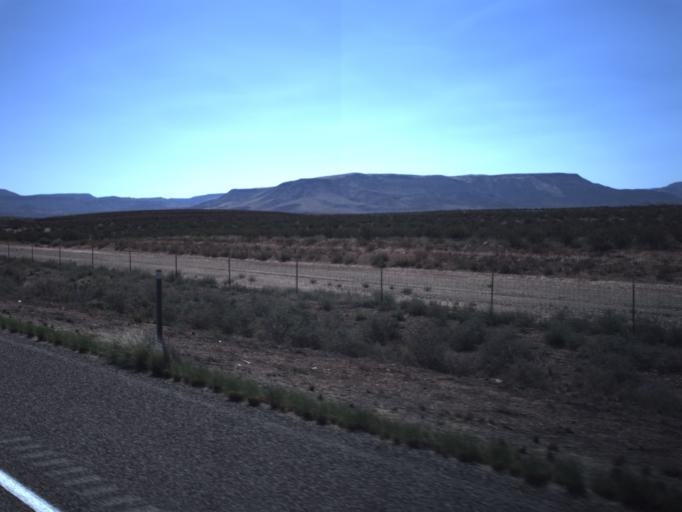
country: US
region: Utah
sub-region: Washington County
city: Saint George
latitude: 37.0134
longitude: -113.5929
